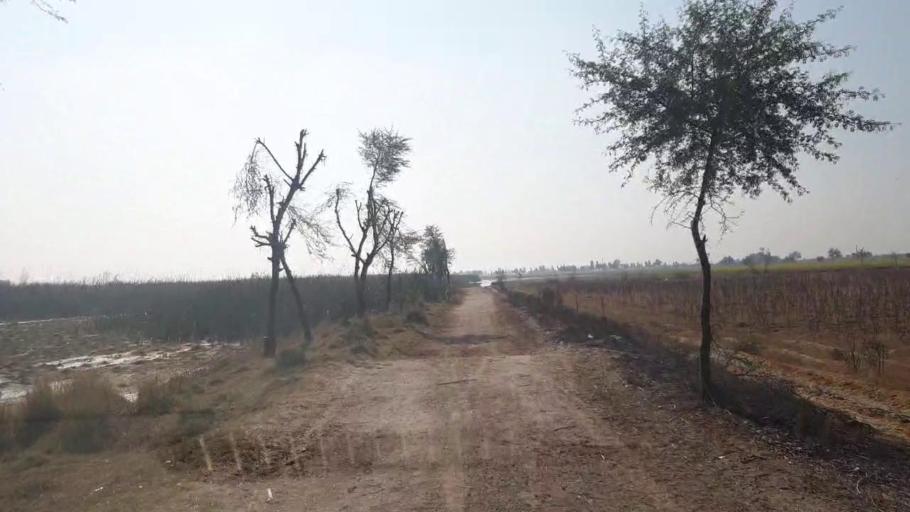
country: PK
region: Sindh
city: Shahdadpur
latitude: 25.9420
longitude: 68.5442
